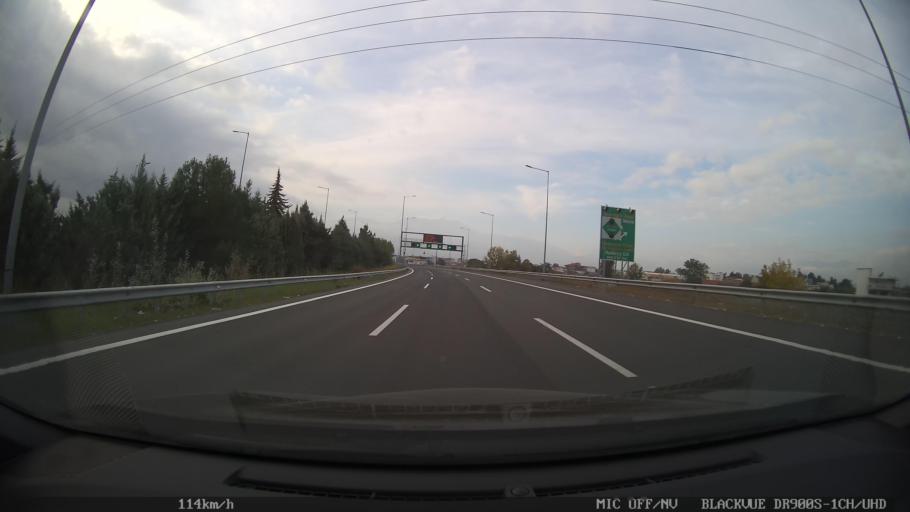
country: GR
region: Central Macedonia
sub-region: Nomos Pierias
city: Peristasi
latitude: 40.2812
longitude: 22.5234
